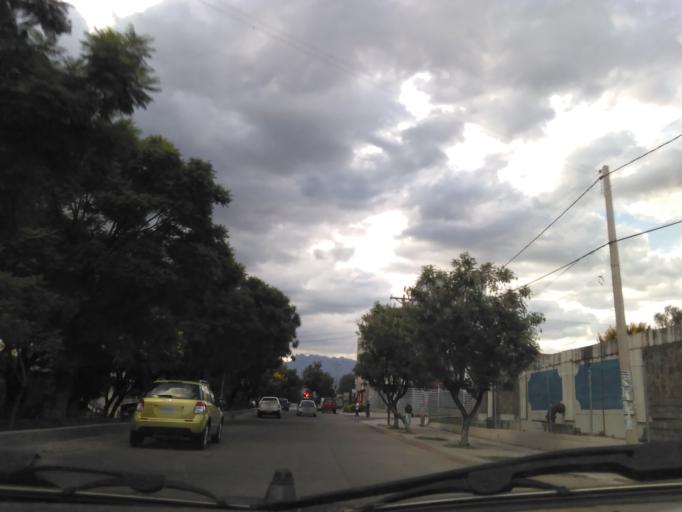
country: BO
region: Cochabamba
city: Cochabamba
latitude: -17.3648
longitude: -66.1630
